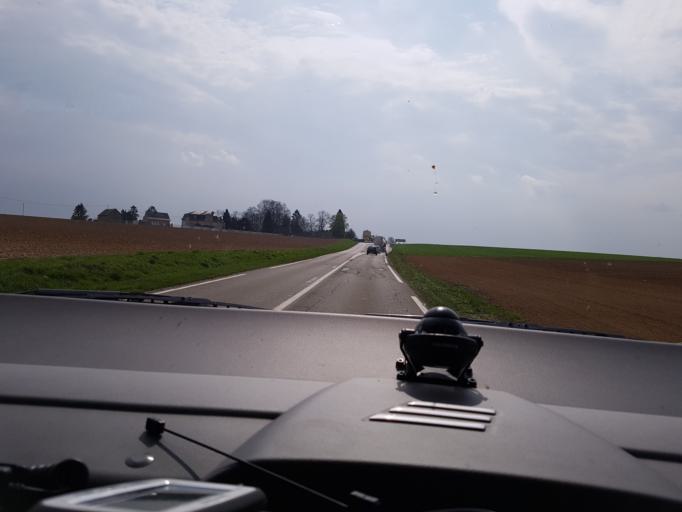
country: FR
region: Picardie
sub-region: Departement de l'Aisne
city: Crouy
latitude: 49.4492
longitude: 3.3571
